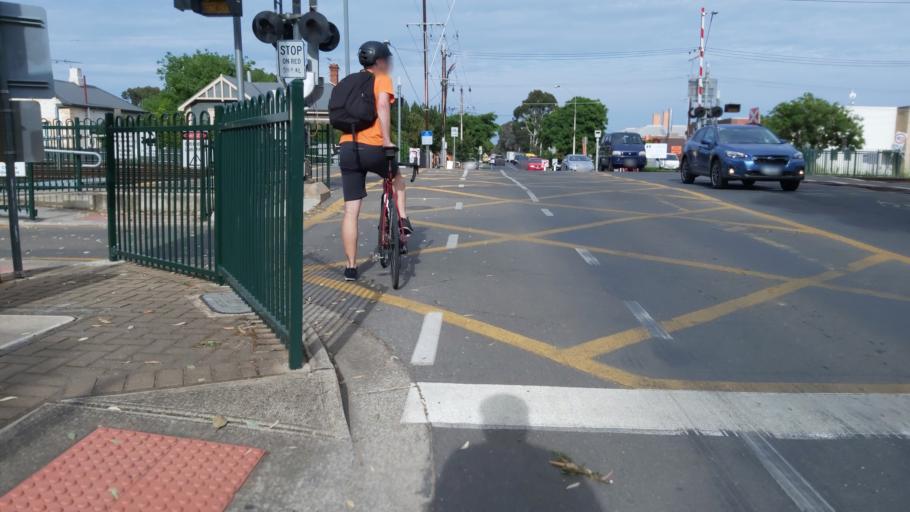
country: AU
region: South Australia
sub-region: Unley
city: Wayville
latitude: -34.9488
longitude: 138.5845
